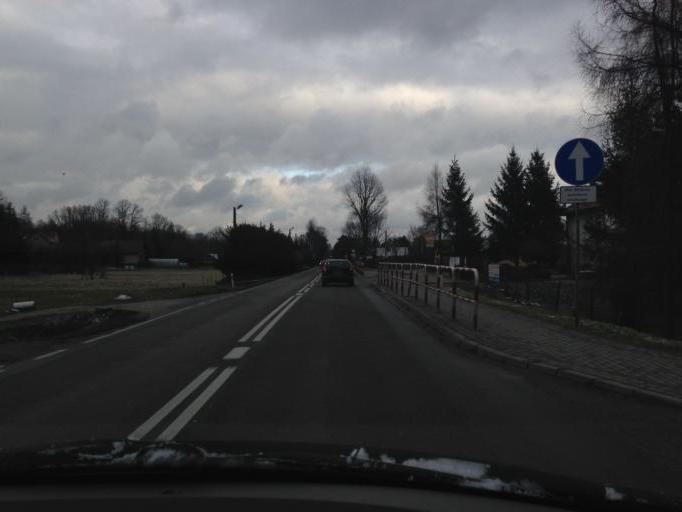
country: PL
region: Lesser Poland Voivodeship
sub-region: Powiat myslenicki
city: Dobczyce
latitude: 49.9011
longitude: 20.1397
